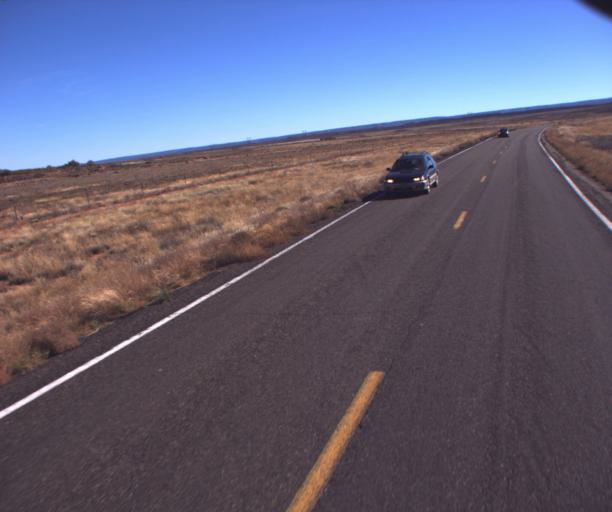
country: US
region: Arizona
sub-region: Coconino County
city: Fredonia
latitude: 36.9219
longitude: -112.4431
